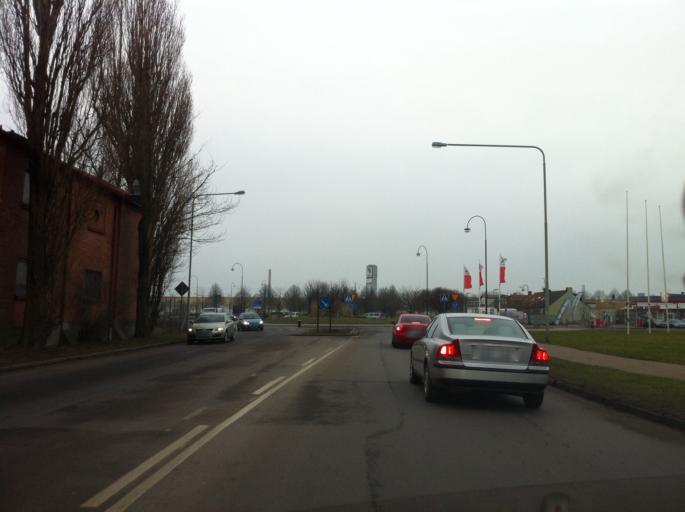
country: SE
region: Skane
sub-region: Landskrona
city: Landskrona
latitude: 55.8732
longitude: 12.8503
